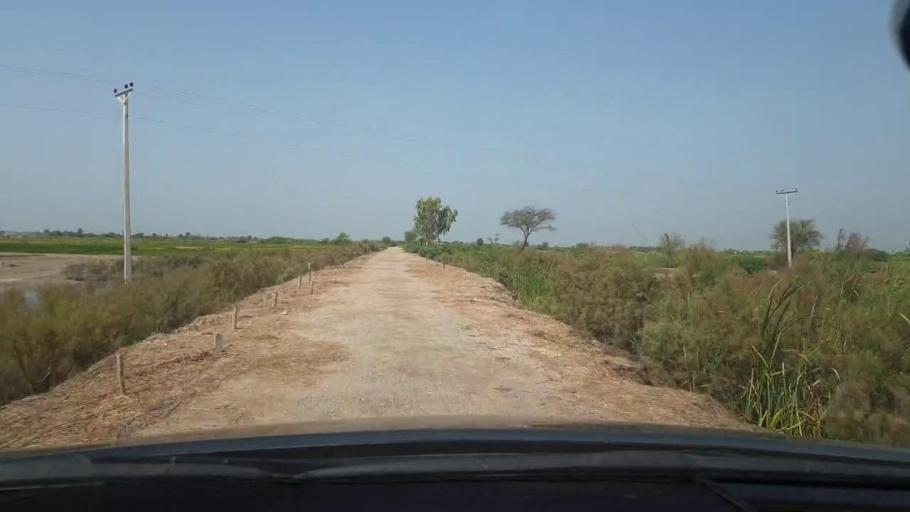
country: PK
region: Sindh
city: Tando Bago
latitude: 24.7092
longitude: 69.1151
